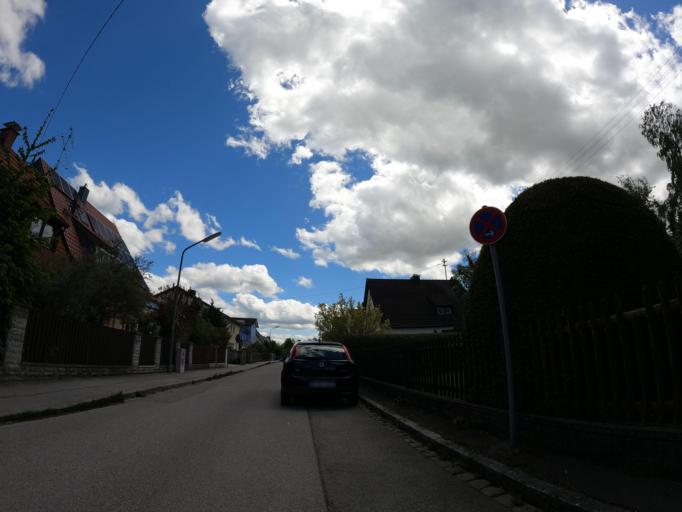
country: DE
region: Bavaria
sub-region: Upper Bavaria
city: Kirchheim bei Muenchen
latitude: 48.1606
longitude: 11.7588
